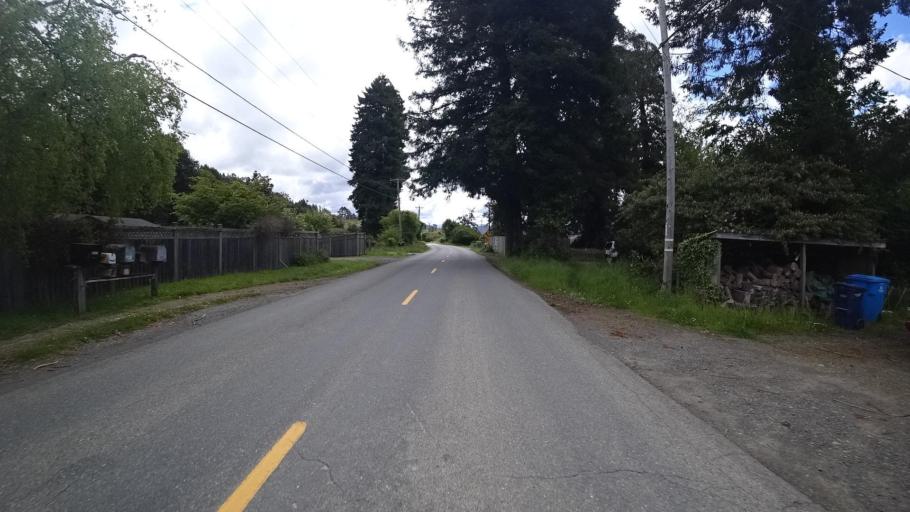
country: US
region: California
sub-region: Humboldt County
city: Blue Lake
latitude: 40.8944
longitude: -124.0041
